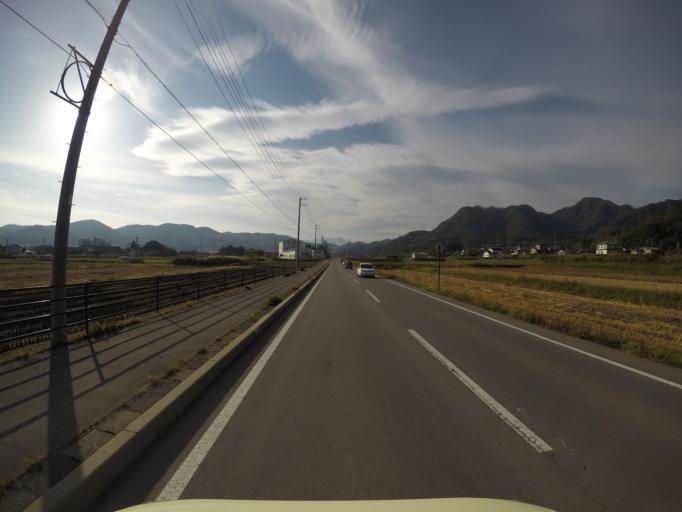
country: JP
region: Nagano
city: Kamimaruko
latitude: 36.3423
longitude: 138.2642
